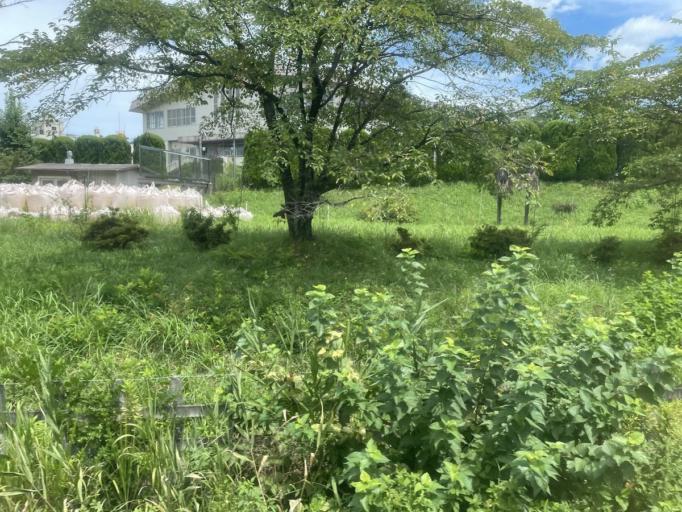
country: JP
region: Saitama
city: Chichibu
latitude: 35.9781
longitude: 139.1045
